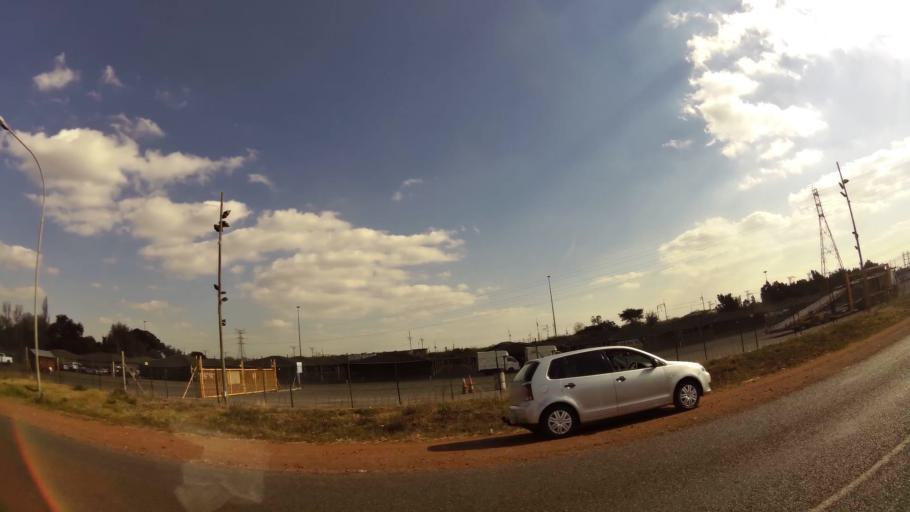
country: ZA
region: Gauteng
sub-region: Ekurhuleni Metropolitan Municipality
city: Tembisa
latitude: -26.0170
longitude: 28.2556
